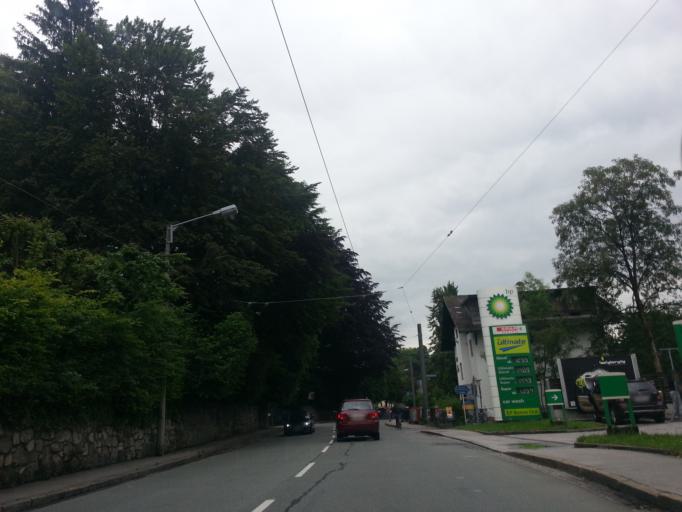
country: AT
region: Salzburg
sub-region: Salzburg Stadt
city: Salzburg
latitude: 47.7972
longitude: 13.0677
